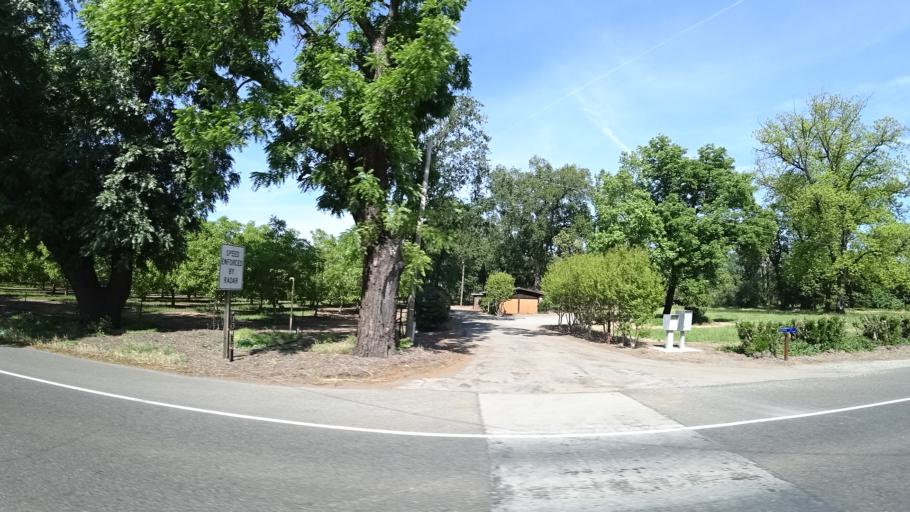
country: US
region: California
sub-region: Tehama County
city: Red Bluff
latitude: 40.1726
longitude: -122.1651
